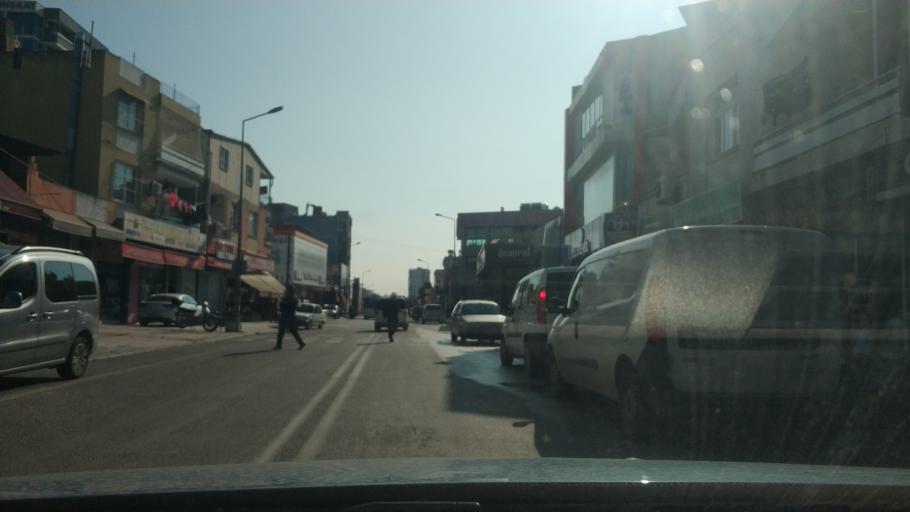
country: TR
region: Adana
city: Seyhan
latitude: 37.0172
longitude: 35.2994
